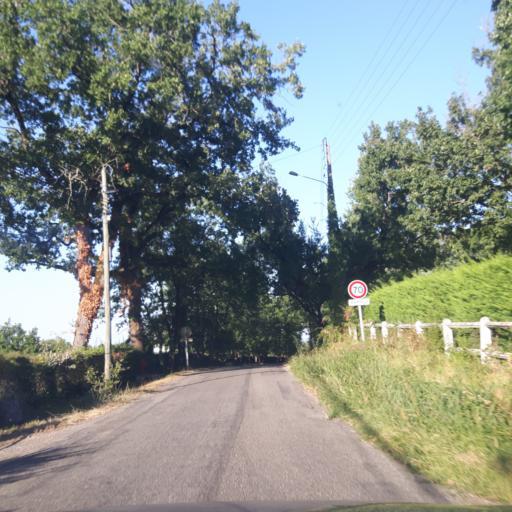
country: FR
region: Midi-Pyrenees
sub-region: Departement de la Haute-Garonne
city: Bouloc
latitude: 43.7968
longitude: 1.4177
